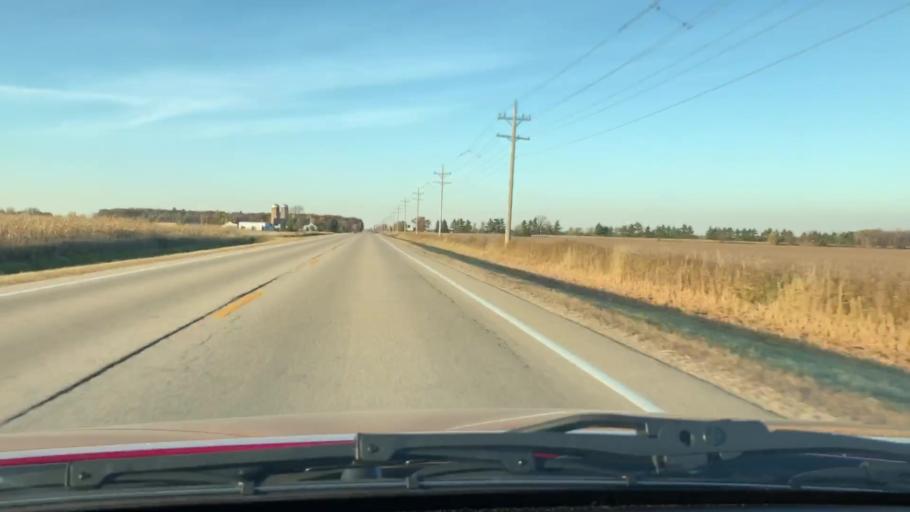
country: US
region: Wisconsin
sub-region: Outagamie County
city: Seymour
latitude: 44.4777
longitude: -88.2910
